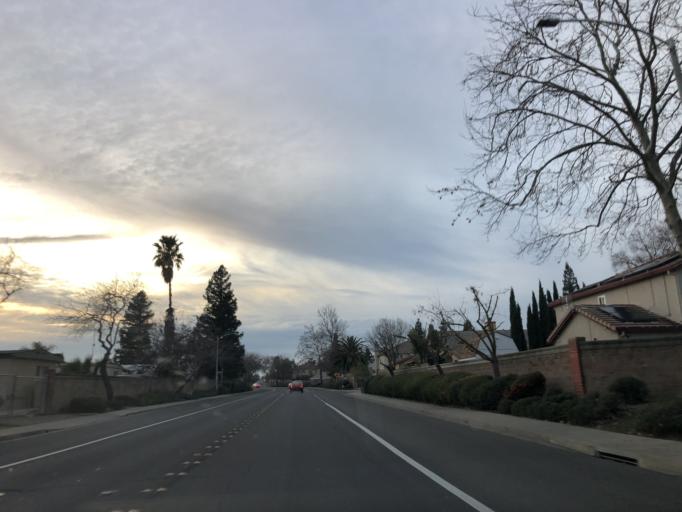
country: US
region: California
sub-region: Yolo County
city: Woodland
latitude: 38.6685
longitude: -121.7441
